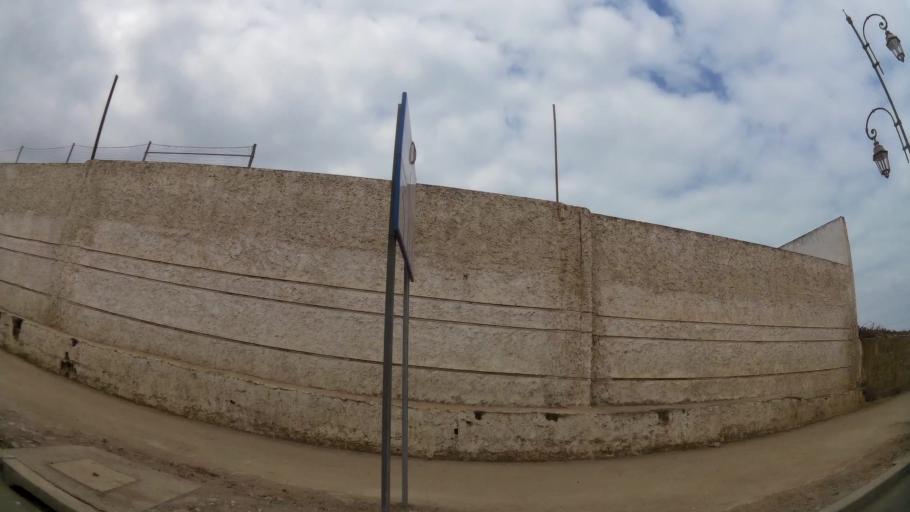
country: MA
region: Rabat-Sale-Zemmour-Zaer
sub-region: Rabat
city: Rabat
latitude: 34.0064
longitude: -6.8647
